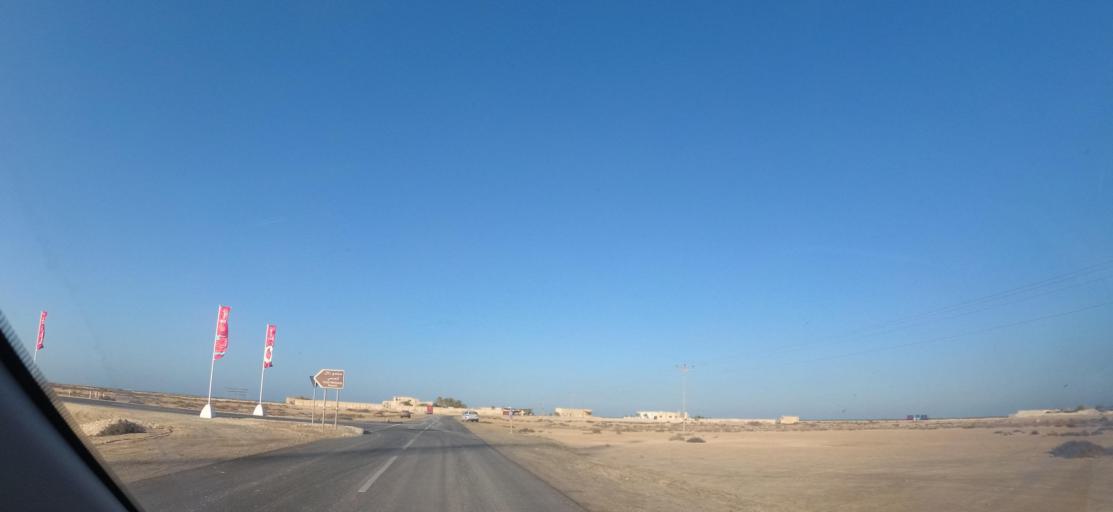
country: QA
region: Madinat ash Shamal
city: Ar Ru'ays
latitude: 26.1543
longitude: 51.2512
